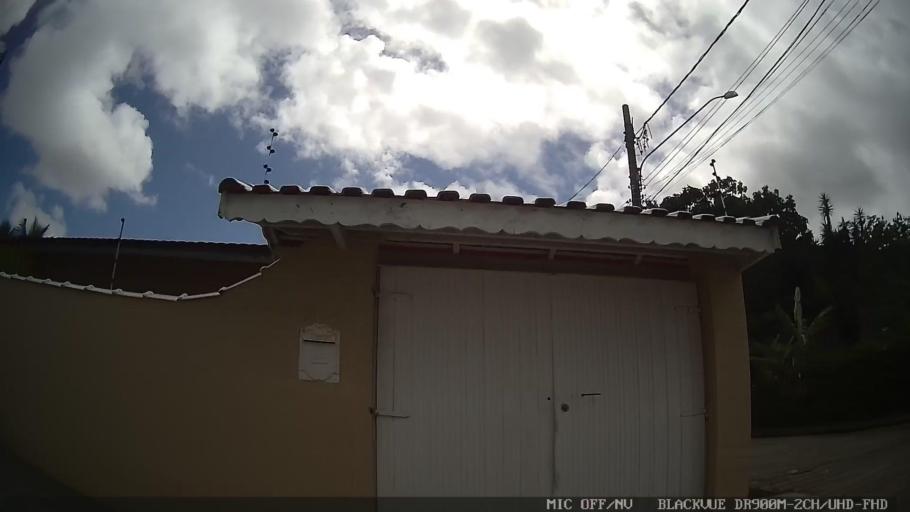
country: BR
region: Sao Paulo
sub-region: Itanhaem
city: Itanhaem
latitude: -24.1933
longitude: -46.8040
